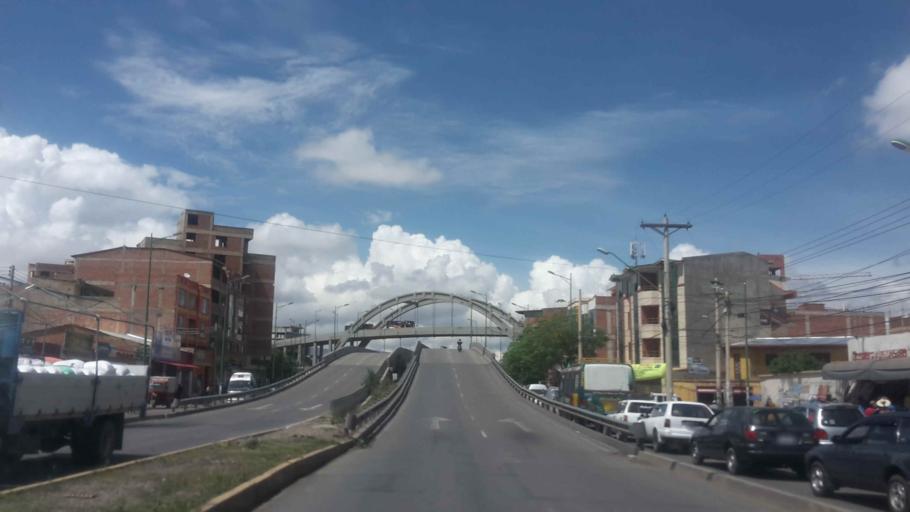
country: BO
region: Cochabamba
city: Cochabamba
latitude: -17.4112
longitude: -66.1520
